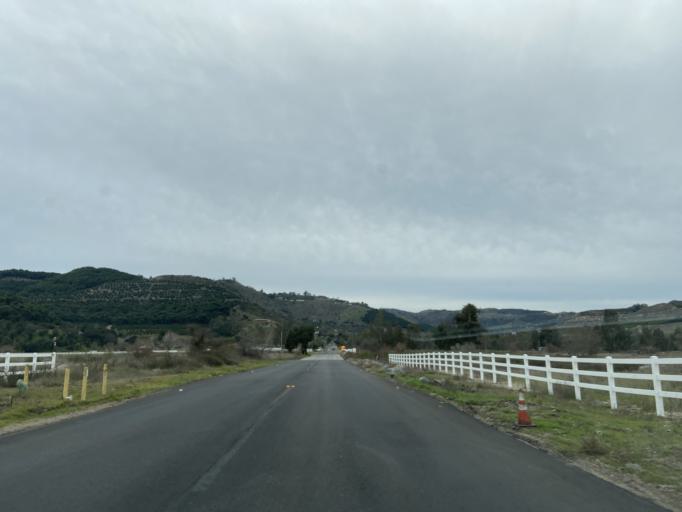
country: US
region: California
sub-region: San Diego County
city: Valley Center
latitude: 33.3141
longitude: -117.0023
